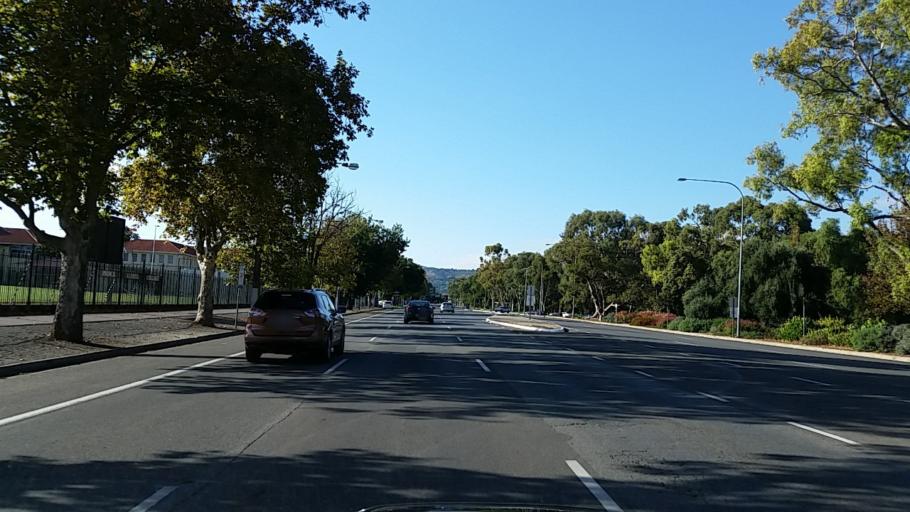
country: AU
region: South Australia
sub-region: Adelaide
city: Adelaide
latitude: -34.9236
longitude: 138.6173
